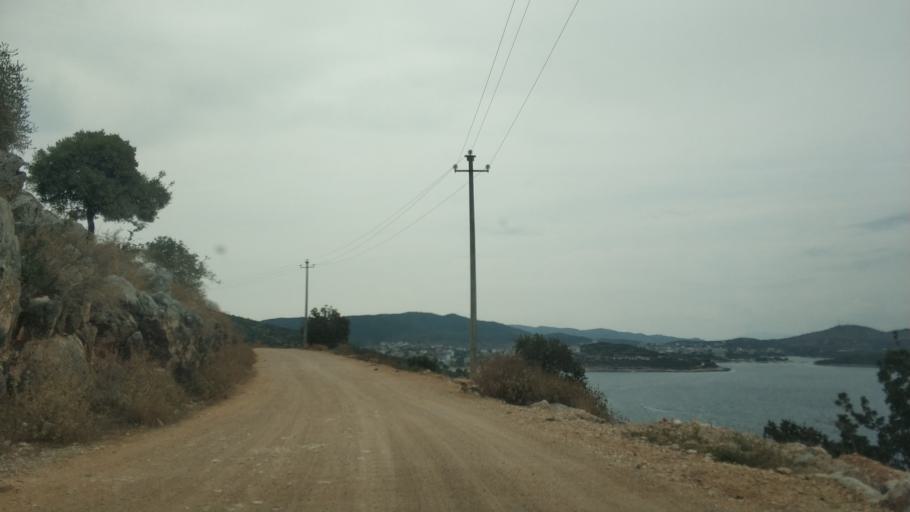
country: AL
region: Vlore
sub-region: Rrethi i Sarandes
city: Xarre
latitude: 39.7927
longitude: 20.0052
